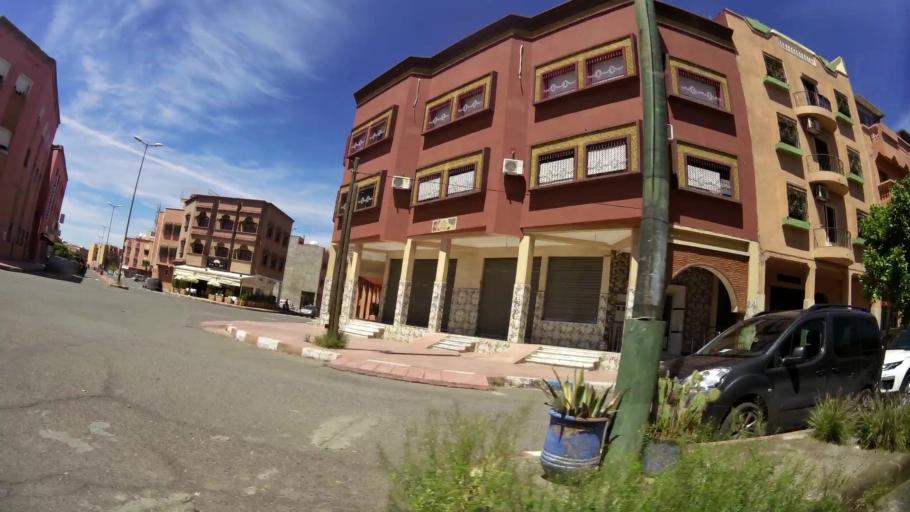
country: MA
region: Marrakech-Tensift-Al Haouz
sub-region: Marrakech
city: Marrakesh
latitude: 31.6403
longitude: -8.0629
